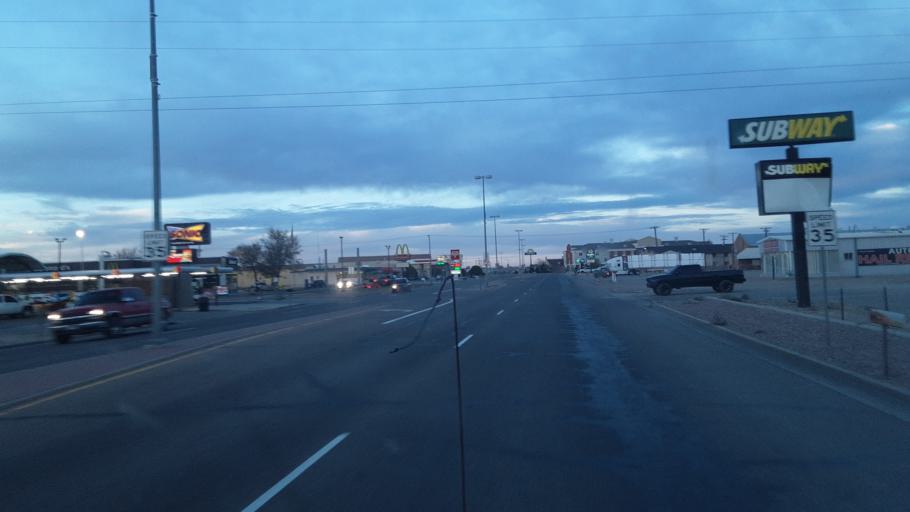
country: US
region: Colorado
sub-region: Prowers County
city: Lamar
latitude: 38.0985
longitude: -102.6190
